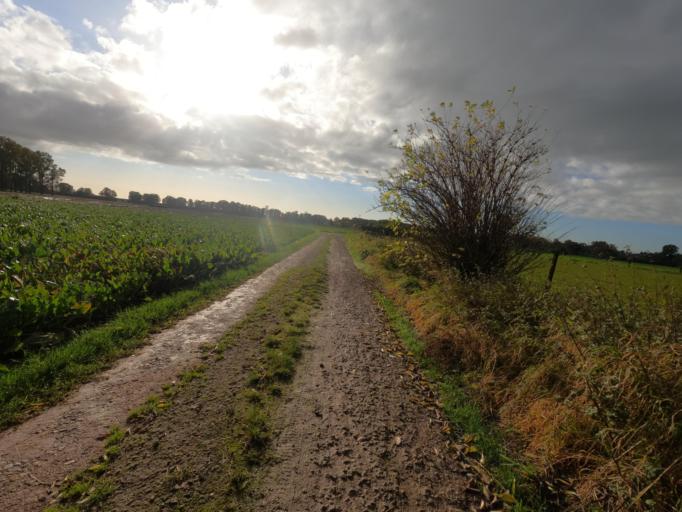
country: DE
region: North Rhine-Westphalia
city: Huckelhoven
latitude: 51.0192
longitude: 6.2352
